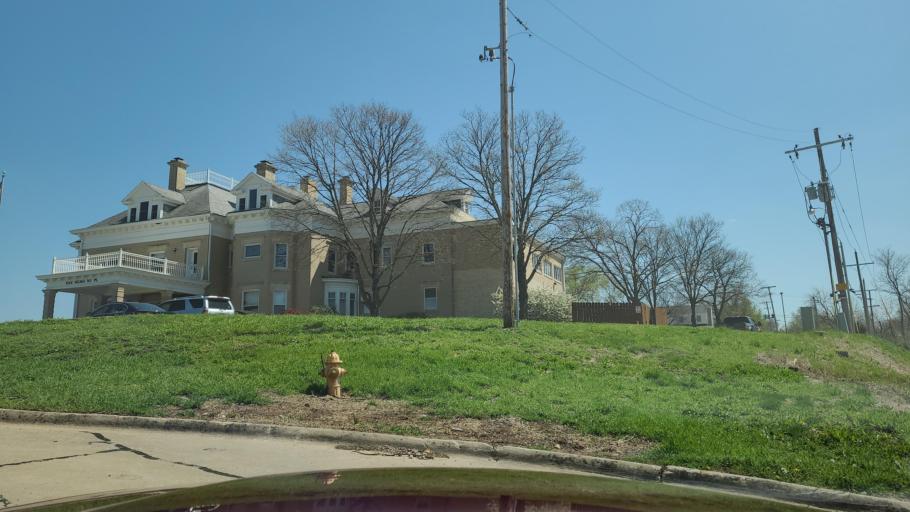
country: US
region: Kansas
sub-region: Douglas County
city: Lawrence
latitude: 38.9655
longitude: -95.2542
